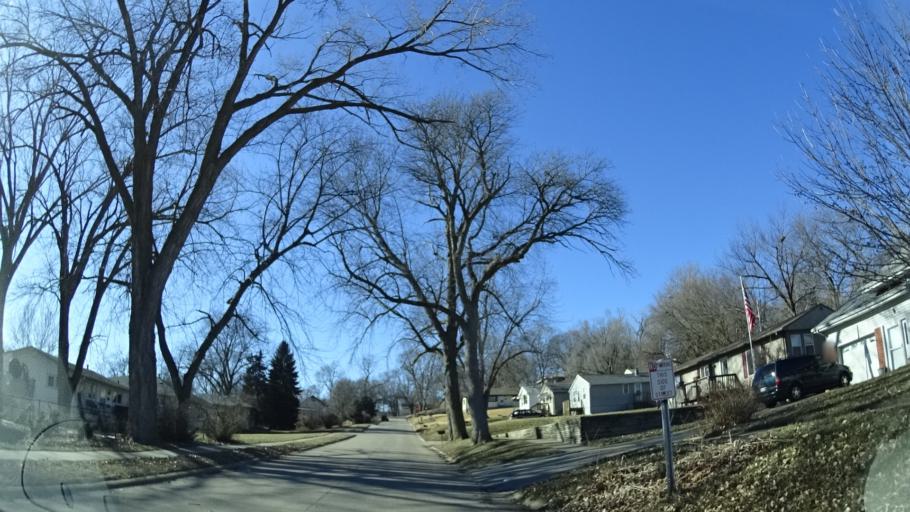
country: US
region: Nebraska
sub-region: Sarpy County
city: Bellevue
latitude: 41.1376
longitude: -95.9003
